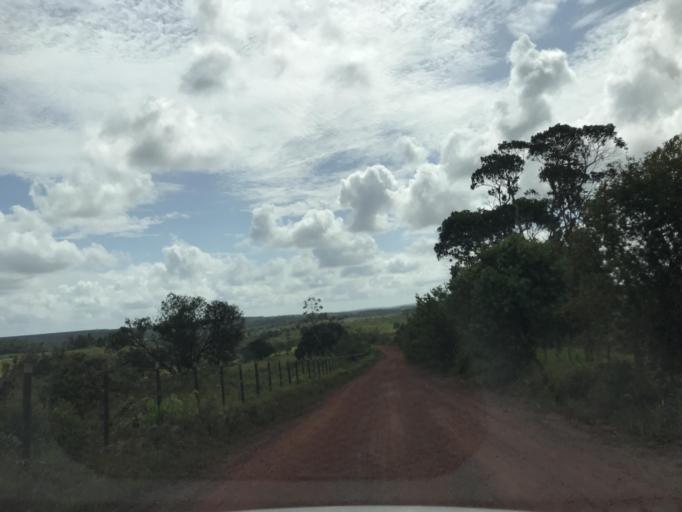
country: BR
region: Bahia
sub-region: Entre Rios
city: Entre Rios
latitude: -12.1699
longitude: -38.1012
